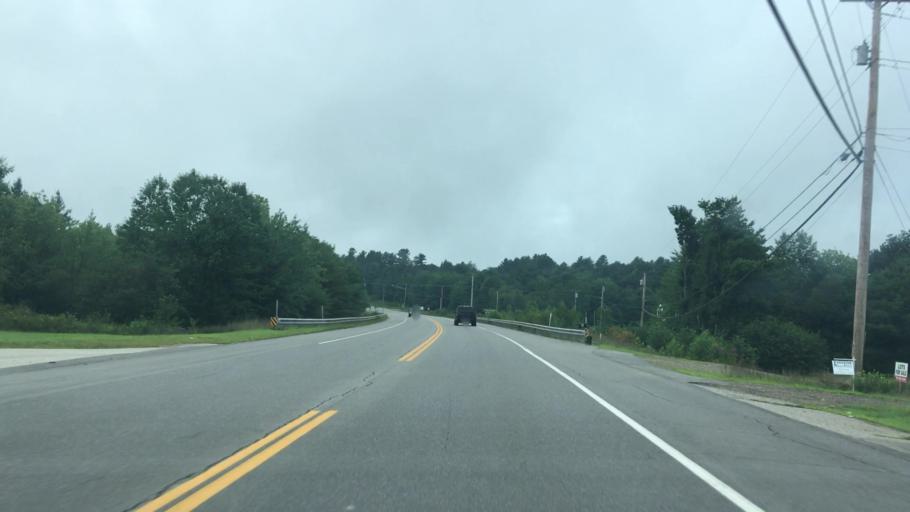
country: US
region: Maine
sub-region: York County
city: Lebanon
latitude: 43.4249
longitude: -70.8497
